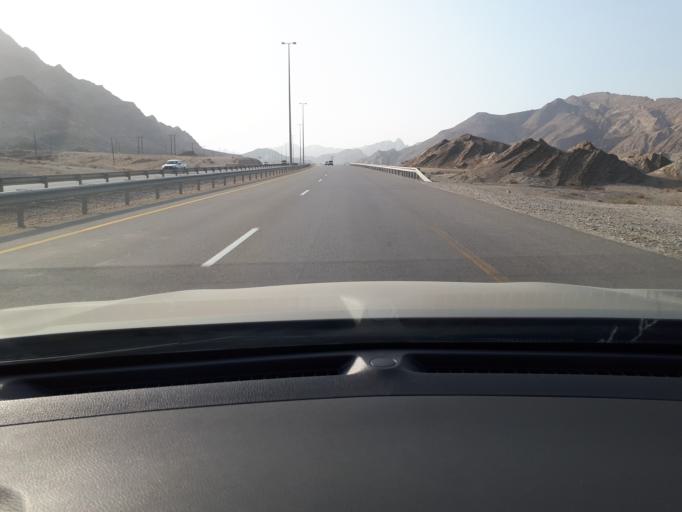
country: OM
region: Muhafazat Masqat
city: Muscat
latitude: 23.3421
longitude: 58.6985
